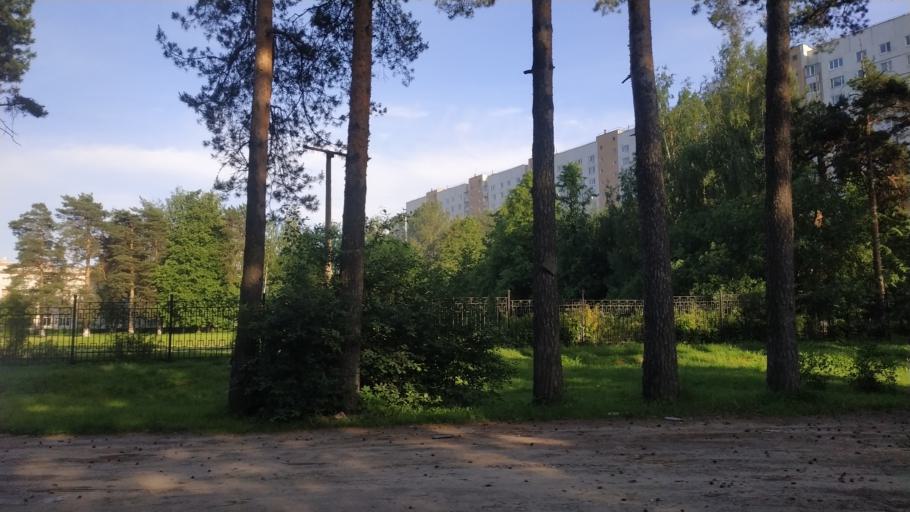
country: RU
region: Moskovskaya
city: Saltykovka
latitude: 55.7300
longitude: 37.9636
